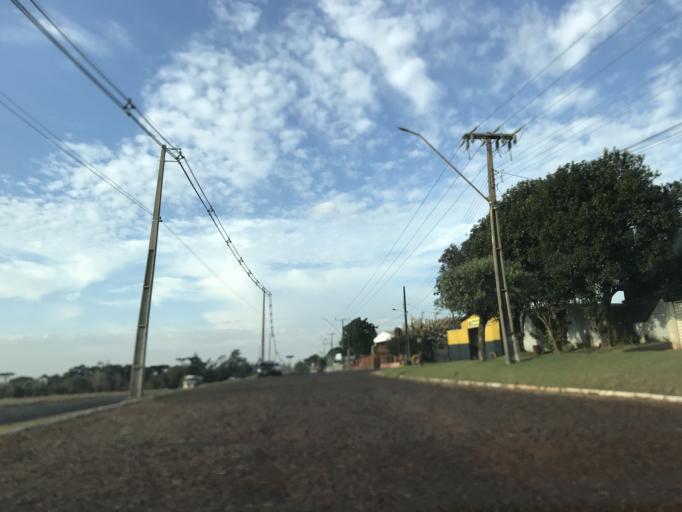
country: BR
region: Parana
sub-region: Cascavel
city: Cascavel
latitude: -25.0471
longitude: -53.6112
